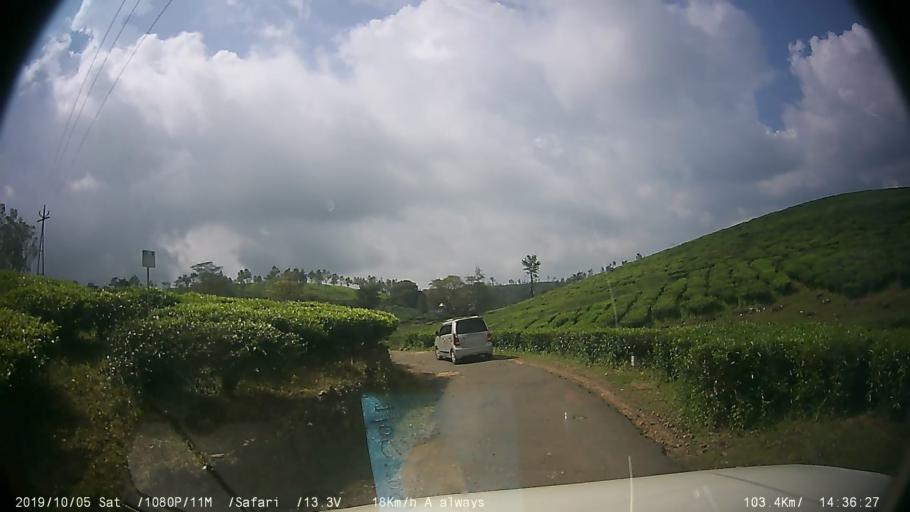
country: IN
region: Kerala
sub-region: Kottayam
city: Erattupetta
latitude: 9.6181
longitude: 76.9610
